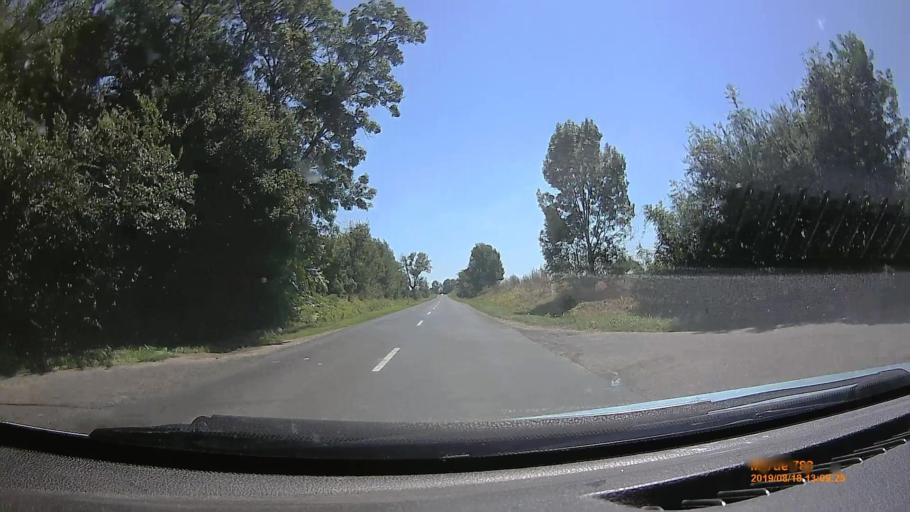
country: HU
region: Fejer
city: Kaloz
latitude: 46.9270
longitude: 18.5102
